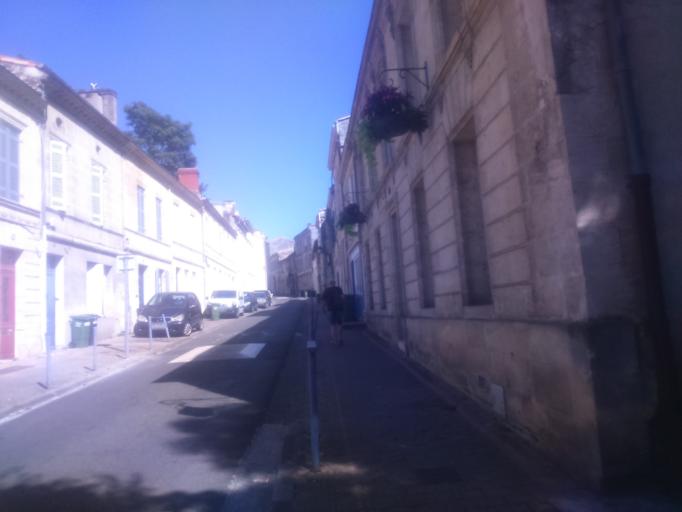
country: FR
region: Aquitaine
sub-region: Departement de la Gironde
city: Lormont
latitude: 44.8777
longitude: -0.5309
